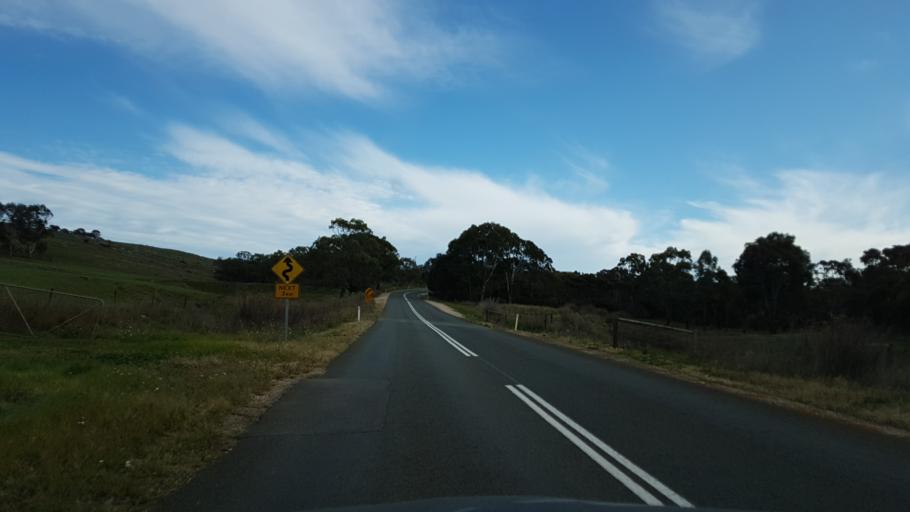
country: AU
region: South Australia
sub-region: Alexandrina
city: Strathalbyn
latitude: -35.1798
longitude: 138.9465
